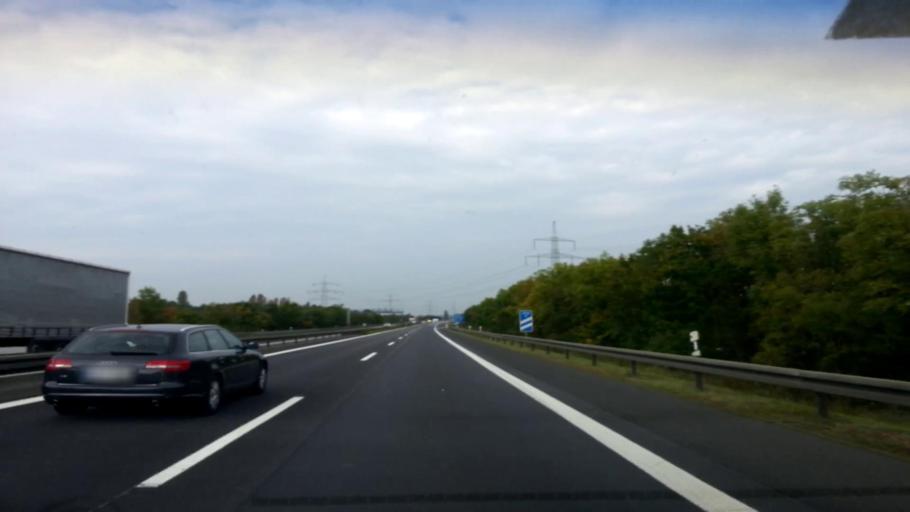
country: DE
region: Bavaria
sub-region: Regierungsbezirk Unterfranken
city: Knetzgau
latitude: 49.9771
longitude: 10.5673
